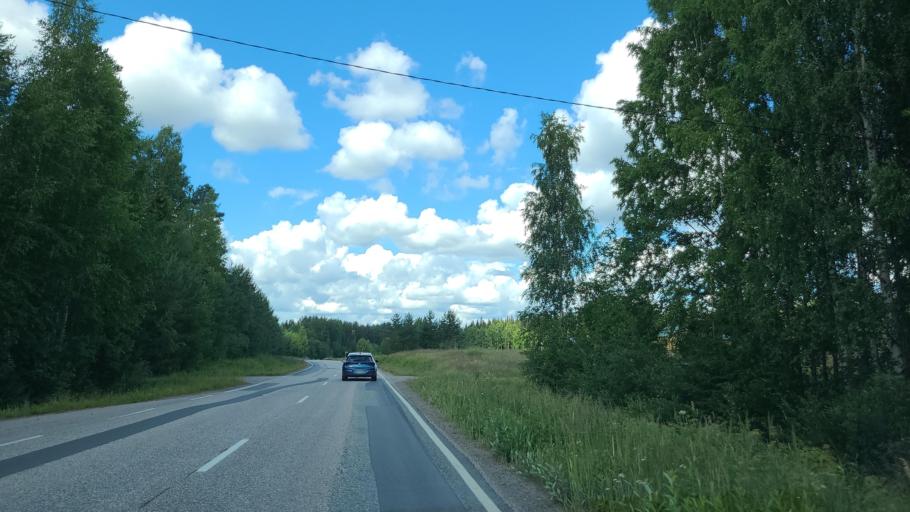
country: FI
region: Northern Savo
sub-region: Koillis-Savo
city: Kaavi
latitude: 62.9092
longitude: 28.7139
